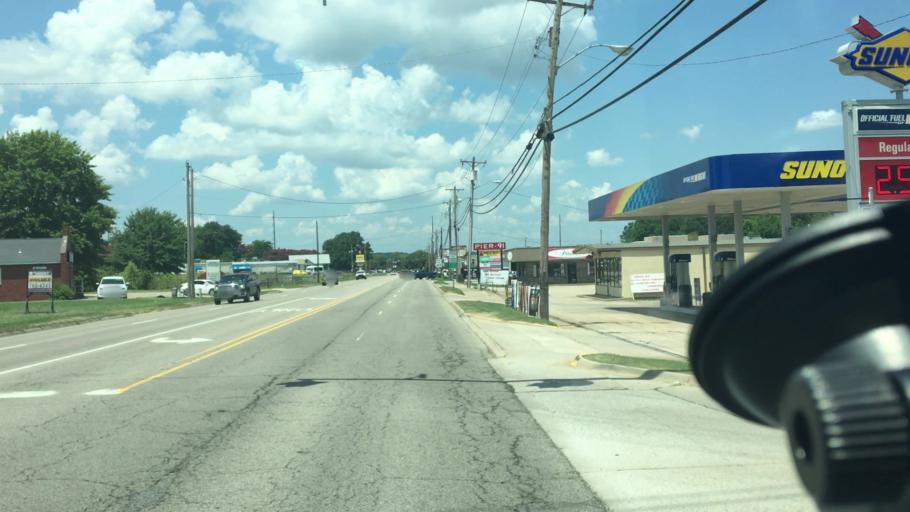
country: US
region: Arkansas
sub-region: Sebastian County
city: Barling
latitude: 35.3452
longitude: -94.3318
